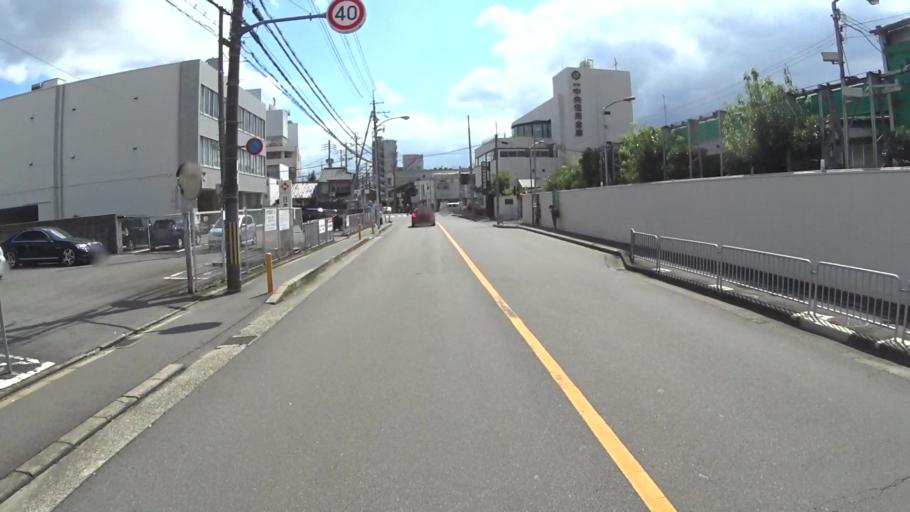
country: JP
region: Kyoto
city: Uji
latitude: 34.9338
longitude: 135.7583
